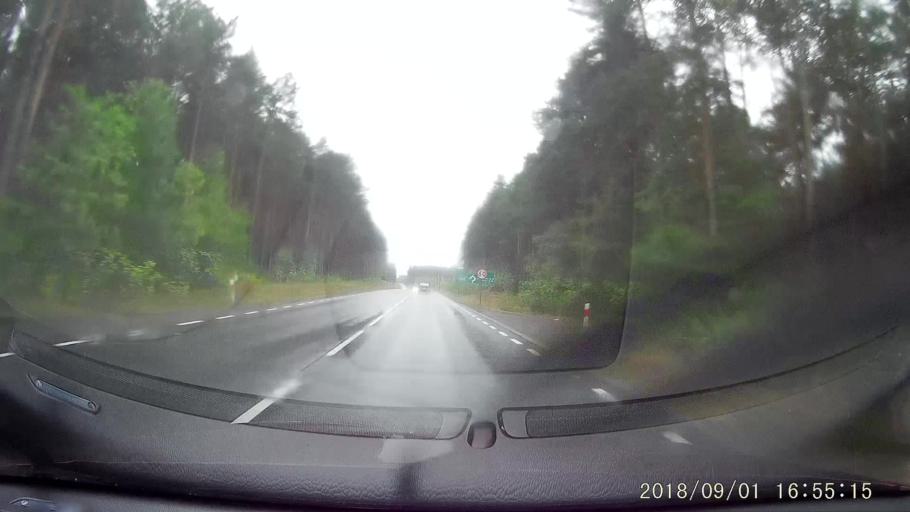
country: PL
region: Lubusz
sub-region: Zielona Gora
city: Zielona Gora
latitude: 51.9496
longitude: 15.4424
